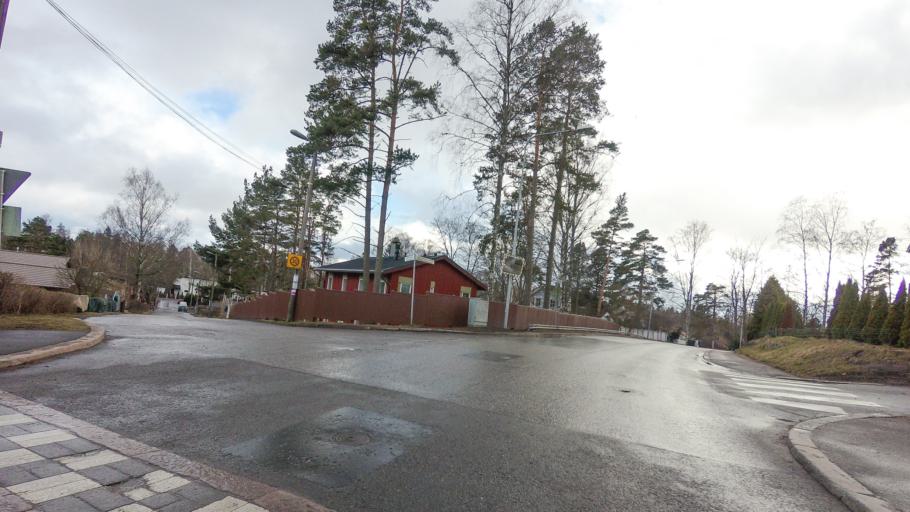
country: FI
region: Uusimaa
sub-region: Helsinki
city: Vantaa
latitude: 60.2059
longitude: 25.0930
